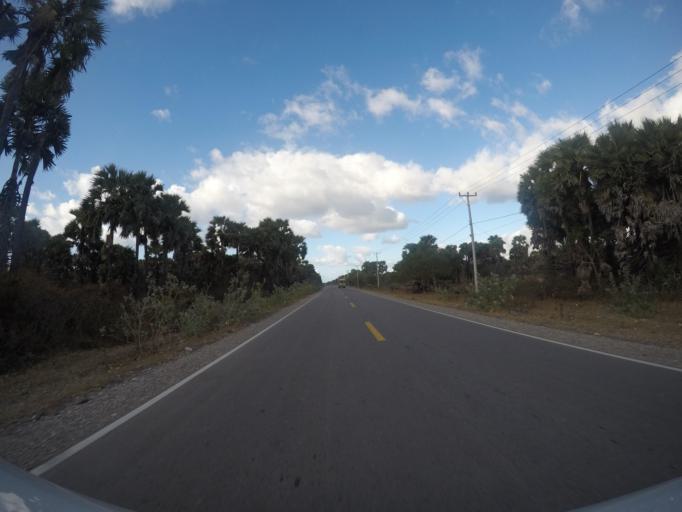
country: TL
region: Lautem
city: Lospalos
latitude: -8.3896
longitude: 126.8507
